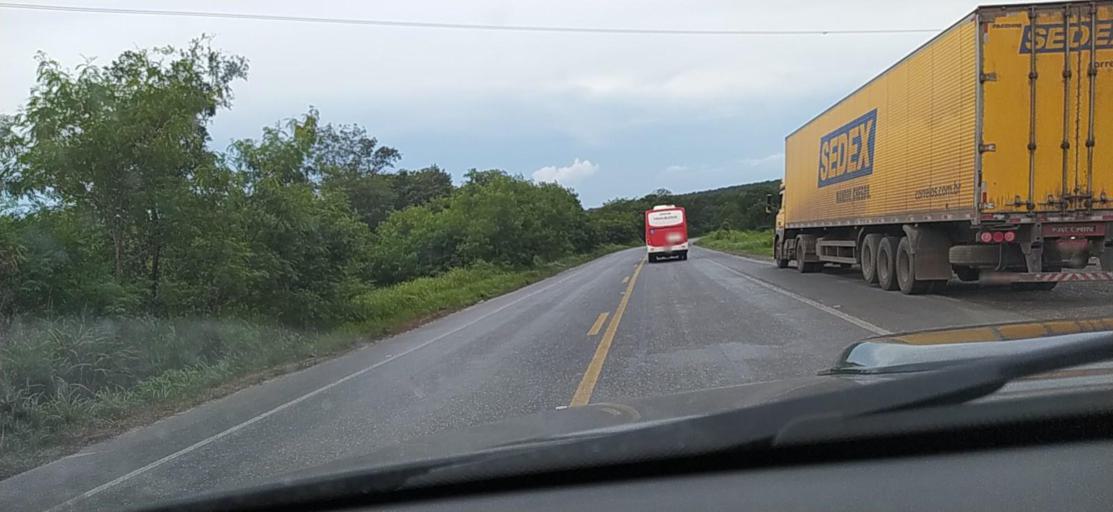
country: BR
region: Minas Gerais
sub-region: Montes Claros
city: Montes Claros
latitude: -16.6659
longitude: -43.7857
